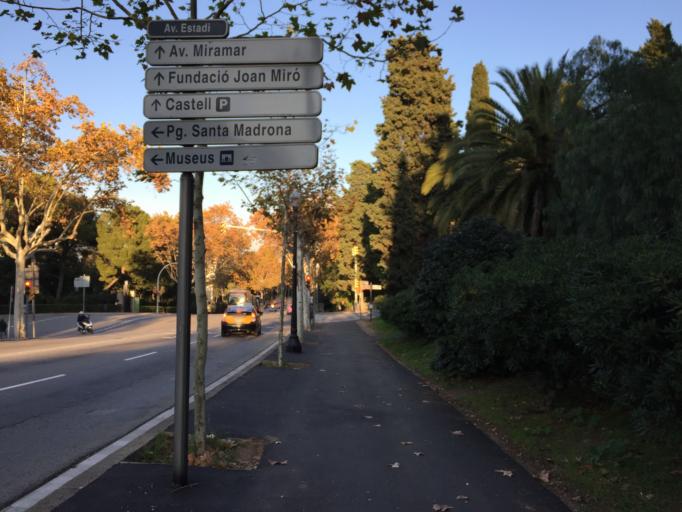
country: ES
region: Catalonia
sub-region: Provincia de Barcelona
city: Sants-Montjuic
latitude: 41.3670
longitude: 2.1586
